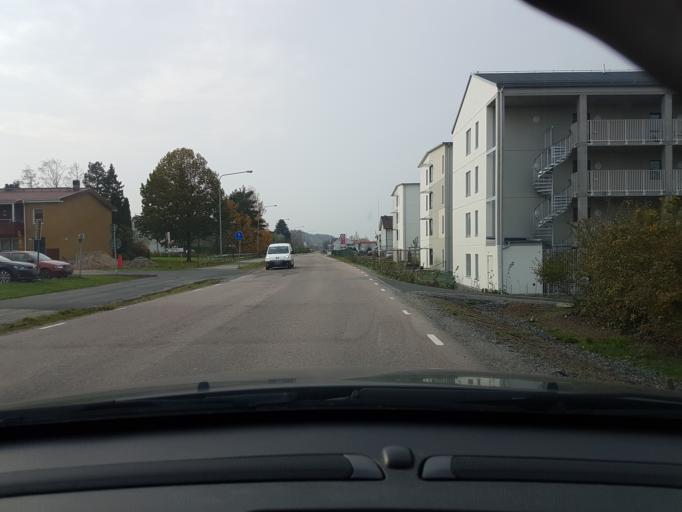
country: SE
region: Vaestra Goetaland
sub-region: Ale Kommun
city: Alvangen
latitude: 57.9612
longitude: 12.1294
